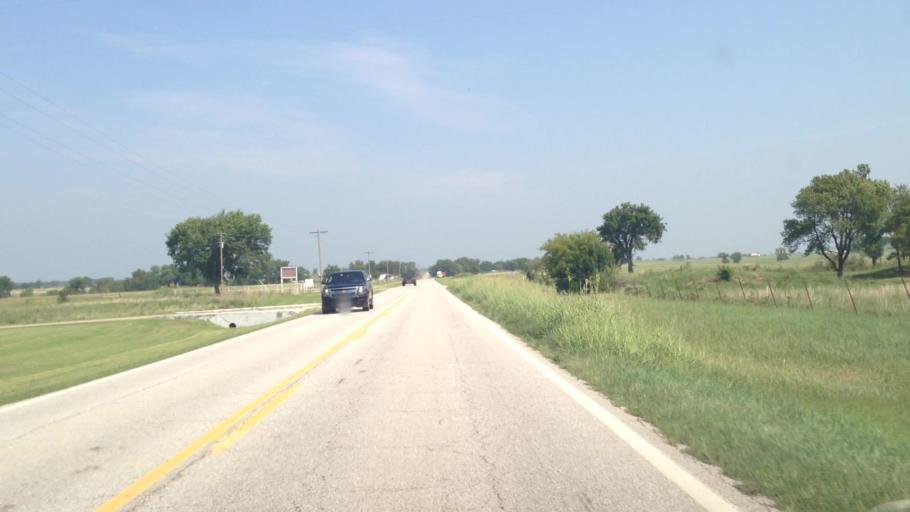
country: US
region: Oklahoma
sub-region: Craig County
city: Vinita
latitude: 36.8143
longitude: -95.1435
